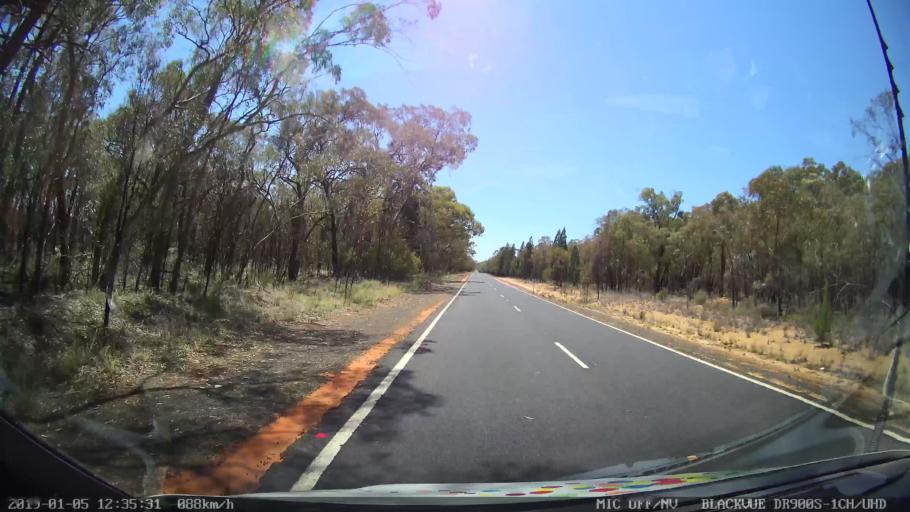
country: AU
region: New South Wales
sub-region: Warrumbungle Shire
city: Coonabarabran
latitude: -31.2094
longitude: 149.4270
